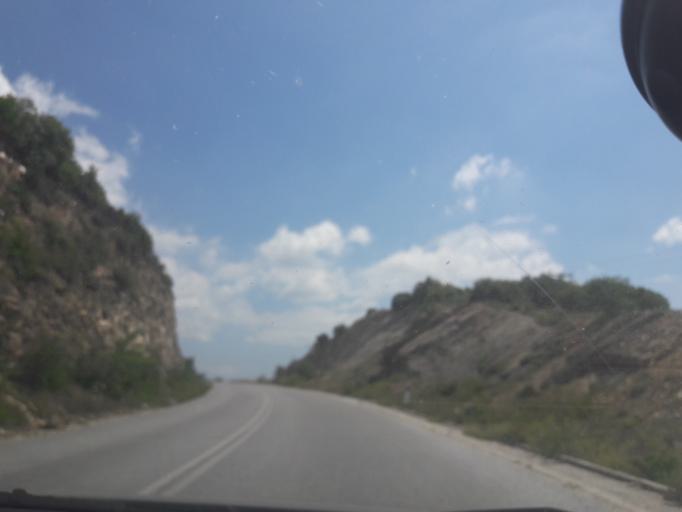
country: GR
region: Central Macedonia
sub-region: Nomos Chalkidikis
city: Polygyros
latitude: 40.3687
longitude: 23.4592
